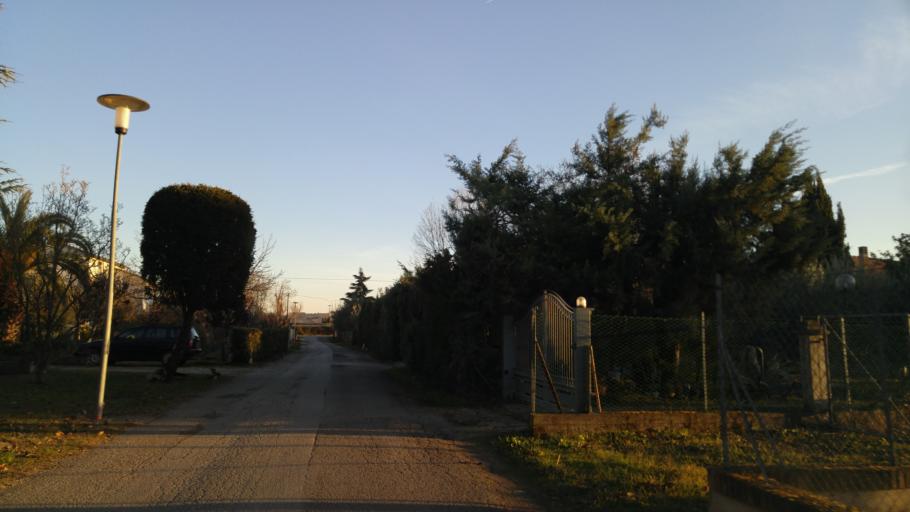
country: IT
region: The Marches
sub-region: Provincia di Pesaro e Urbino
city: Bellocchi
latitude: 43.8033
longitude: 13.0103
